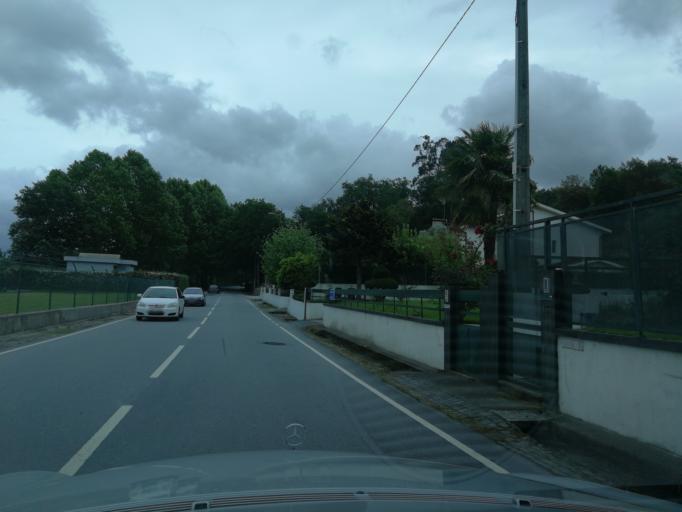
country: PT
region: Braga
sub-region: Braga
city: Adaufe
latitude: 41.6038
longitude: -8.4246
